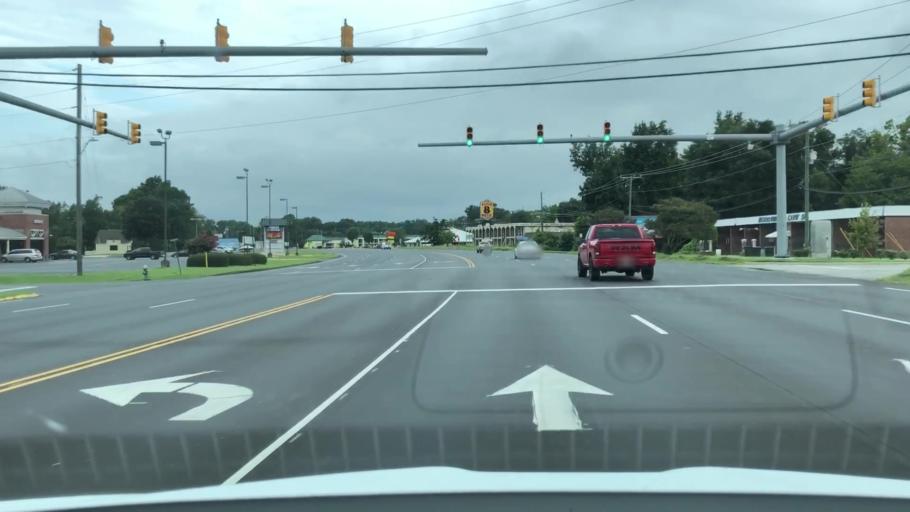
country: US
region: North Carolina
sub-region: Lenoir County
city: Kinston
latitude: 35.2422
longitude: -77.5788
